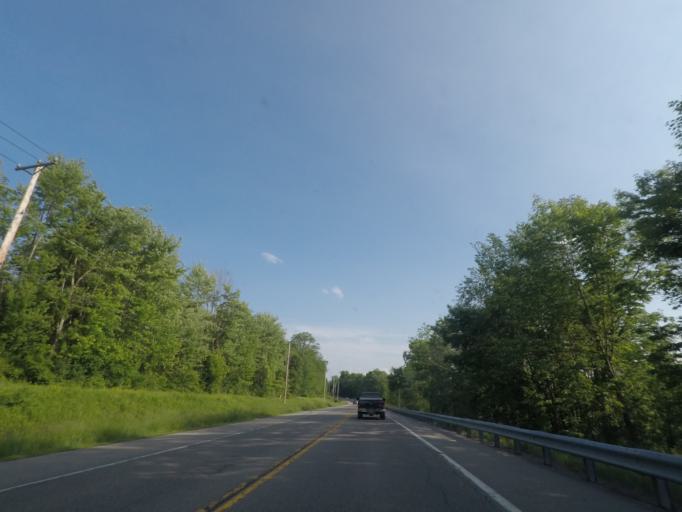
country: US
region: New York
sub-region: Orange County
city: Beaverdam Lake-Salisbury Mills
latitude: 41.4887
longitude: -74.1323
